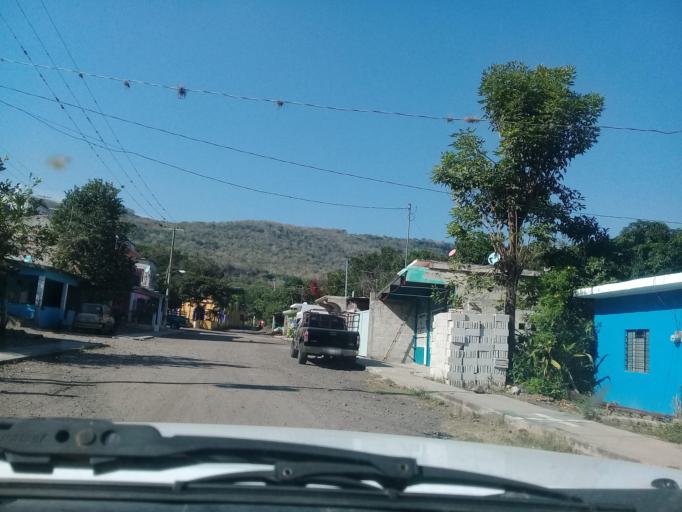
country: MX
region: Veracruz
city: Actopan
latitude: 19.4975
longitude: -96.6079
